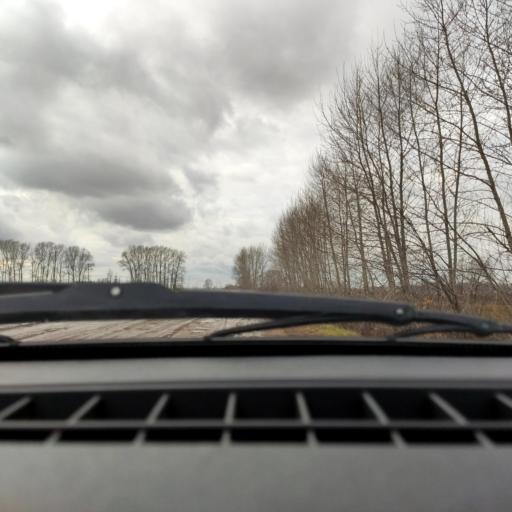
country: RU
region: Bashkortostan
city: Asanovo
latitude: 54.9592
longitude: 55.5724
